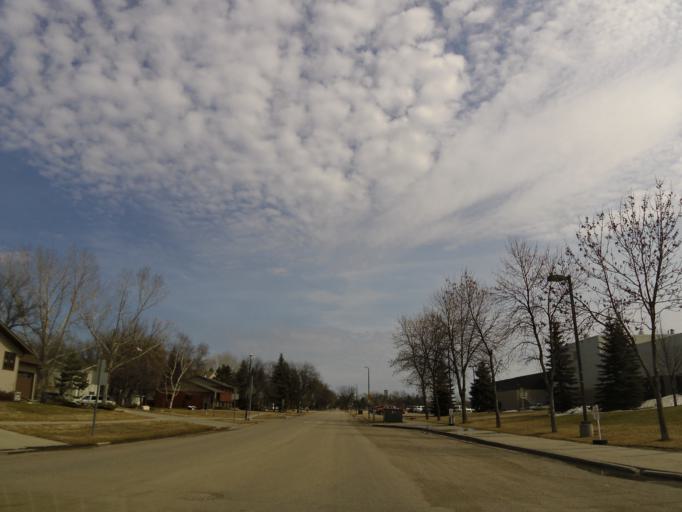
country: US
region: North Dakota
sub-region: Walsh County
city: Grafton
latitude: 48.4082
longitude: -97.4245
